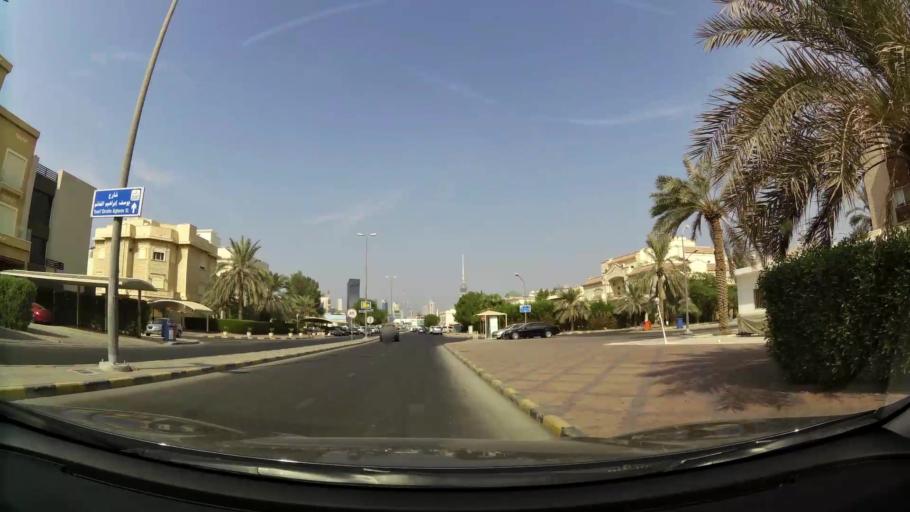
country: KW
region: Al Asimah
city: Ash Shamiyah
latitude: 29.3503
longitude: 47.9640
